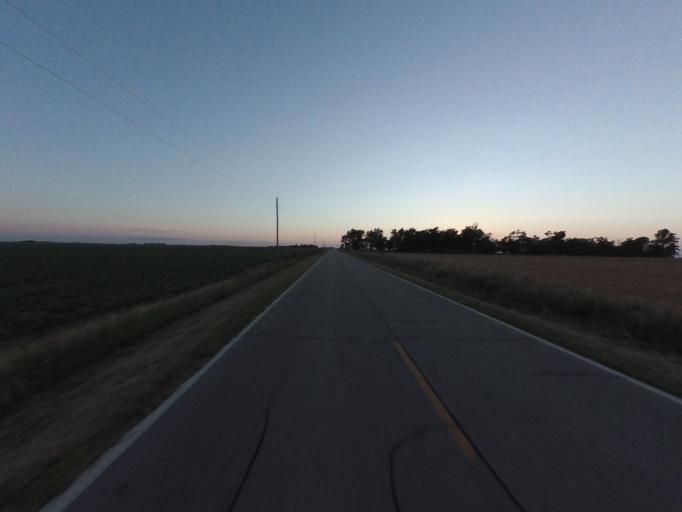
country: US
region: Kansas
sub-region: Rice County
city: Sterling
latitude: 38.1447
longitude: -98.1732
